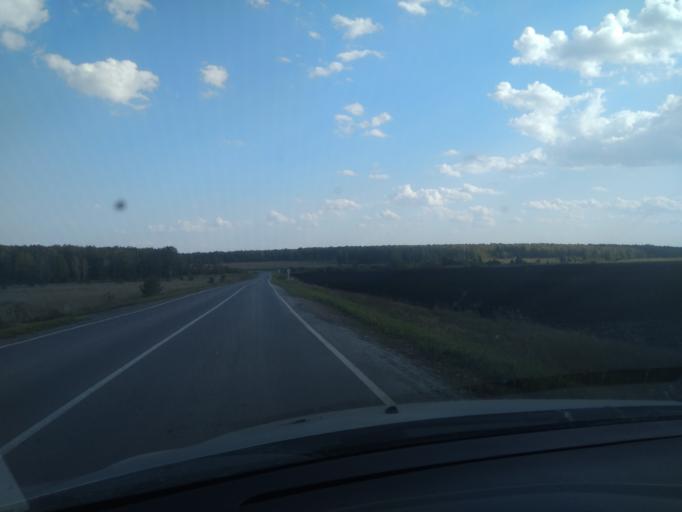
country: RU
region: Sverdlovsk
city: Pokrovskoye
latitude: 56.4236
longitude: 61.6070
